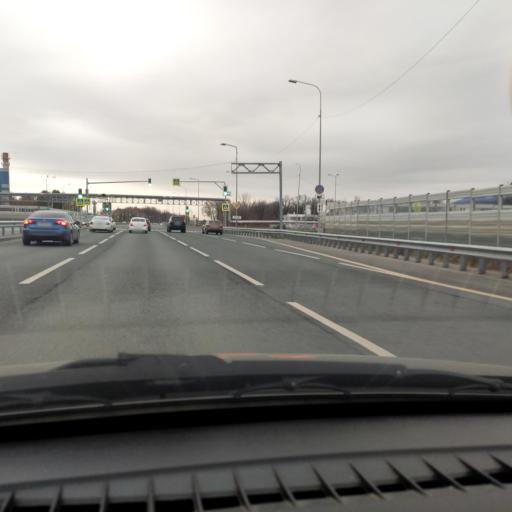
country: RU
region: Samara
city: Bereza
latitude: 53.5123
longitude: 50.1454
